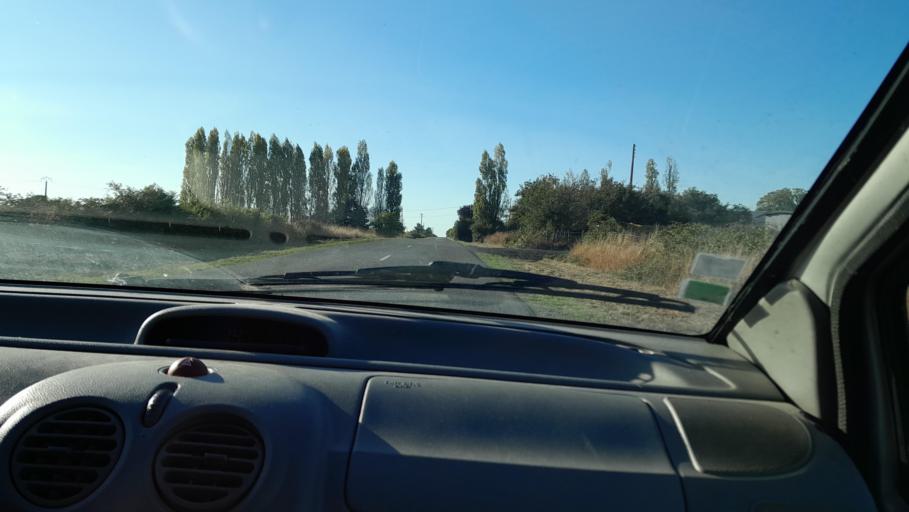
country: FR
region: Pays de la Loire
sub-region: Departement de la Mayenne
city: Craon
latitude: 47.8584
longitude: -0.9742
